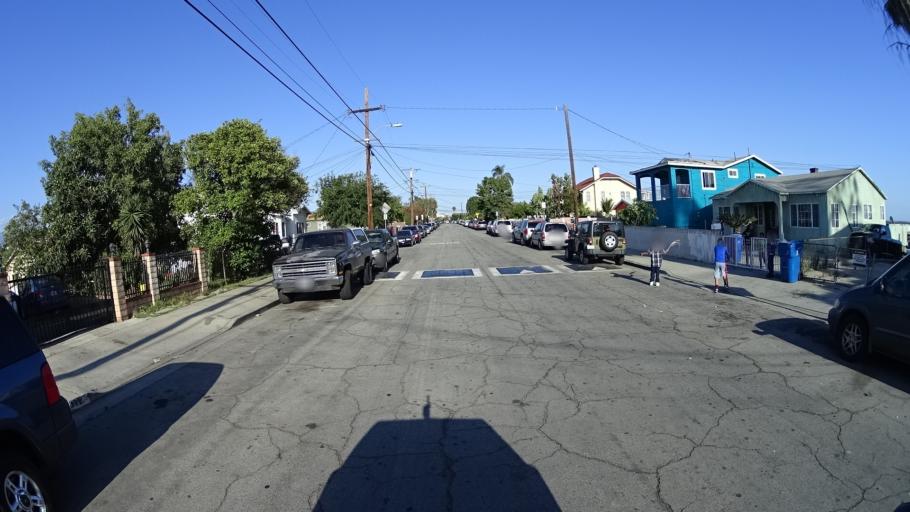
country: US
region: California
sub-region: Los Angeles County
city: Boyle Heights
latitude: 34.0434
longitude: -118.1920
